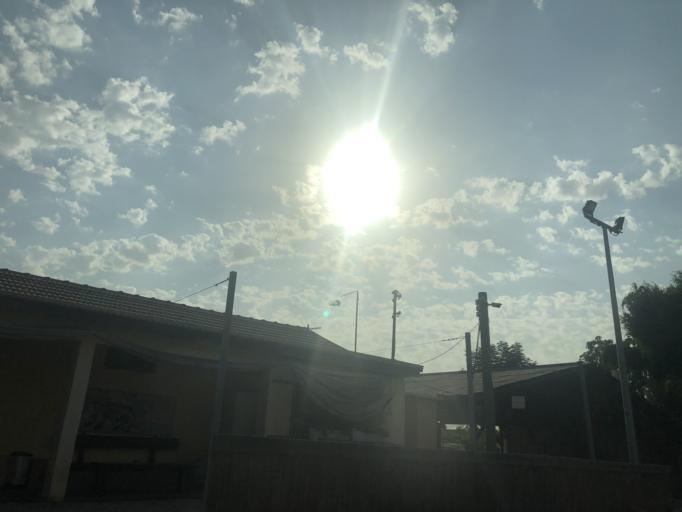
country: IL
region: Central District
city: Rosh Ha'Ayin
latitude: 32.0841
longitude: 34.9347
